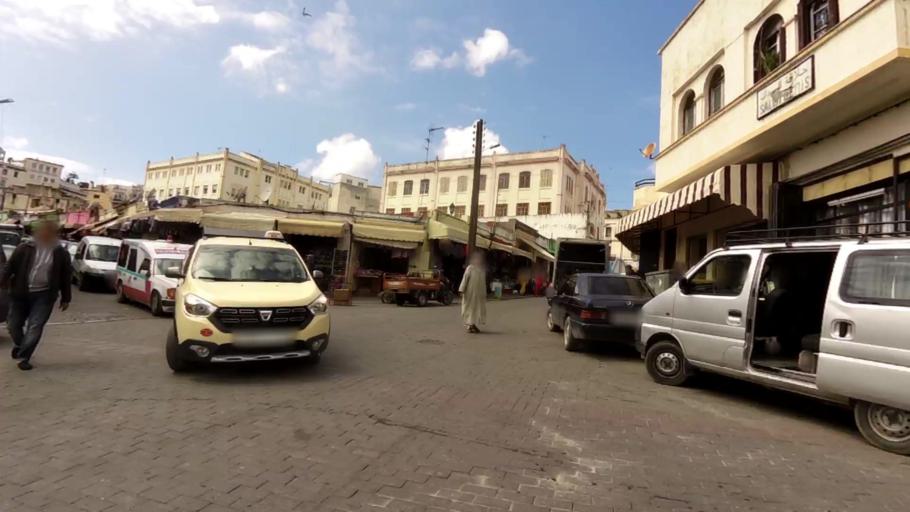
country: MA
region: Tanger-Tetouan
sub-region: Tanger-Assilah
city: Tangier
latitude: 35.7833
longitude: -5.8111
